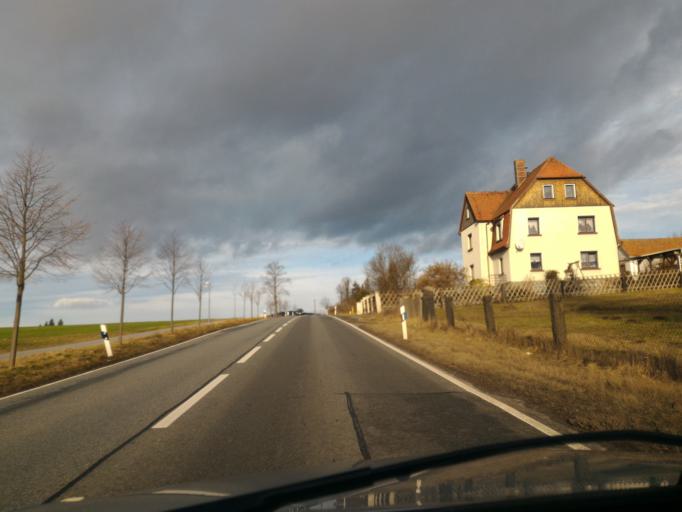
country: DE
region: Saxony
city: Neusalza-Spremberg
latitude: 51.0457
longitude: 14.5139
